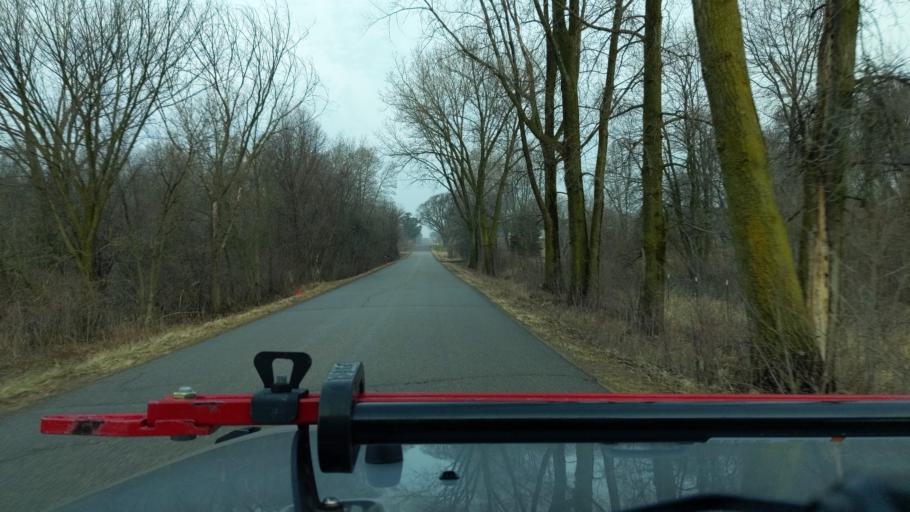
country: US
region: Wisconsin
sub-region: Saint Croix County
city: Hammond
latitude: 44.9343
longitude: -92.4172
